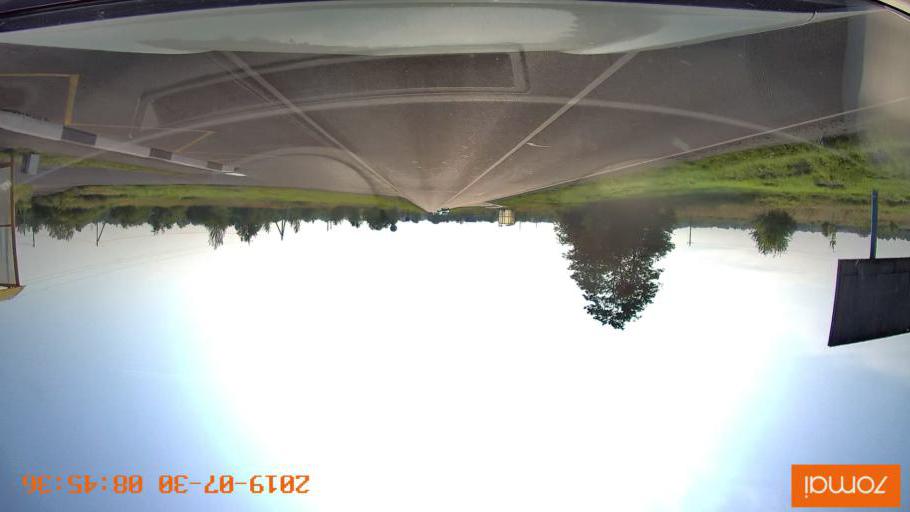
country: RU
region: Kaliningrad
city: Chernyakhovsk
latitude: 54.6259
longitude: 21.8665
